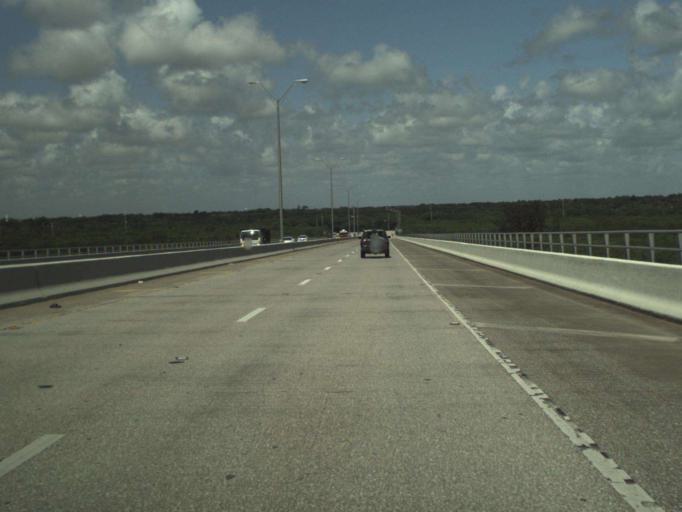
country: US
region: Florida
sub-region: Indian River County
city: Vero Beach
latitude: 27.6525
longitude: -80.3779
